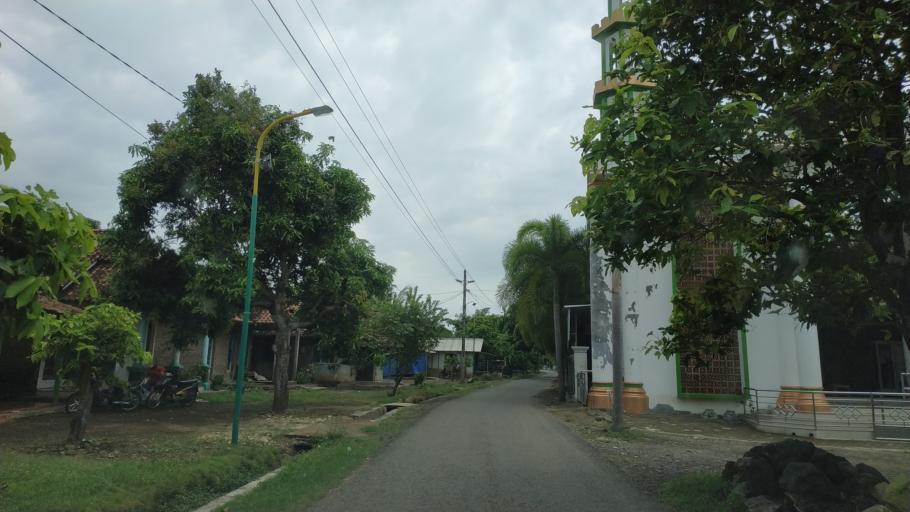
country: ID
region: Central Java
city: Krajan Tegalombo
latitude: -6.4224
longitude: 110.9812
